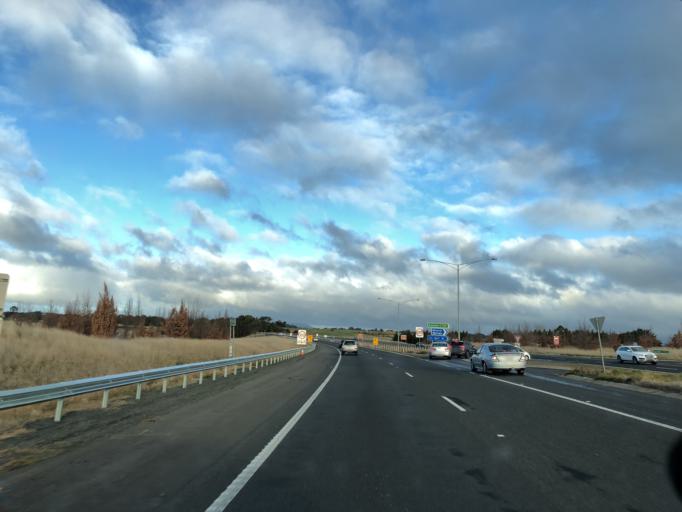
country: AU
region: Victoria
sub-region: Mount Alexander
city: Castlemaine
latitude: -37.2193
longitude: 144.4163
